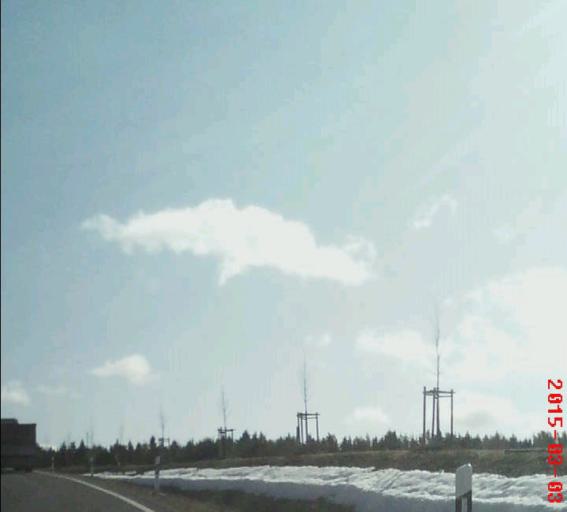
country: DE
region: Thuringia
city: Rottenbach
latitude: 50.7358
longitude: 11.1659
